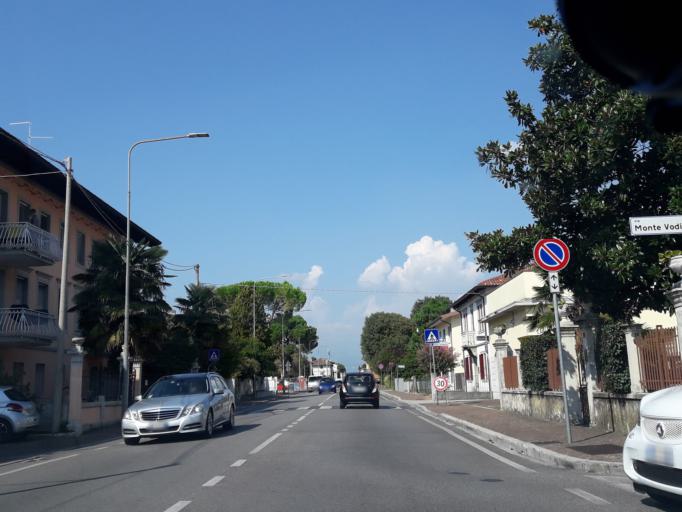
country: IT
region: Friuli Venezia Giulia
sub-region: Provincia di Udine
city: Udine
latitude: 46.0829
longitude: 13.2337
